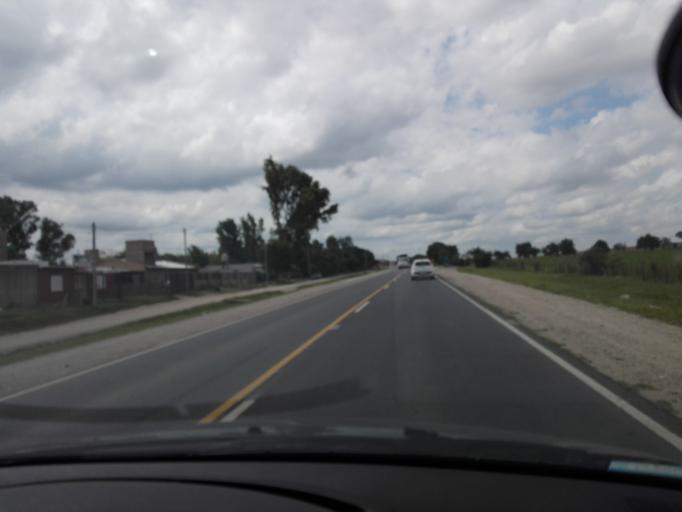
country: AR
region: Cordoba
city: Alta Gracia
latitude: -31.6312
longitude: -64.4355
